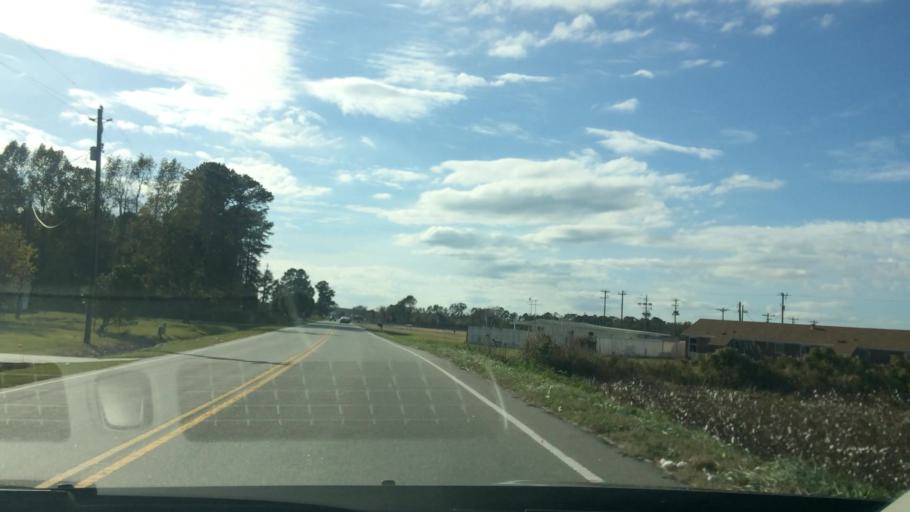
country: US
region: North Carolina
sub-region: Wayne County
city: Elroy
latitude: 35.4416
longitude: -77.8451
